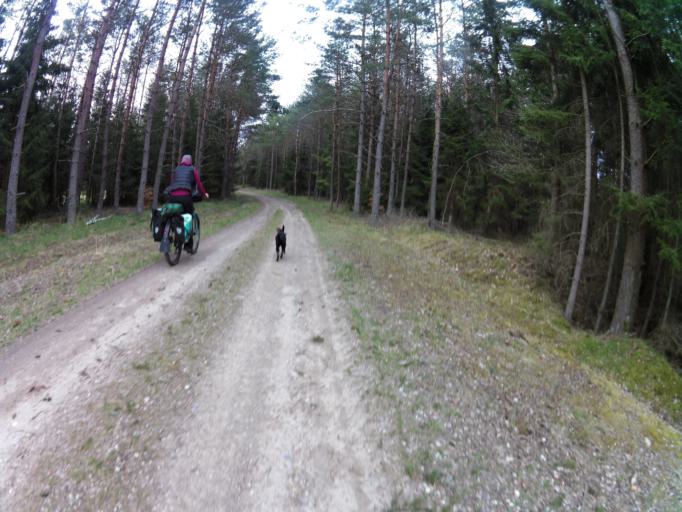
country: PL
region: West Pomeranian Voivodeship
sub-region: Powiat szczecinecki
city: Bialy Bor
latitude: 53.8822
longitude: 16.7192
